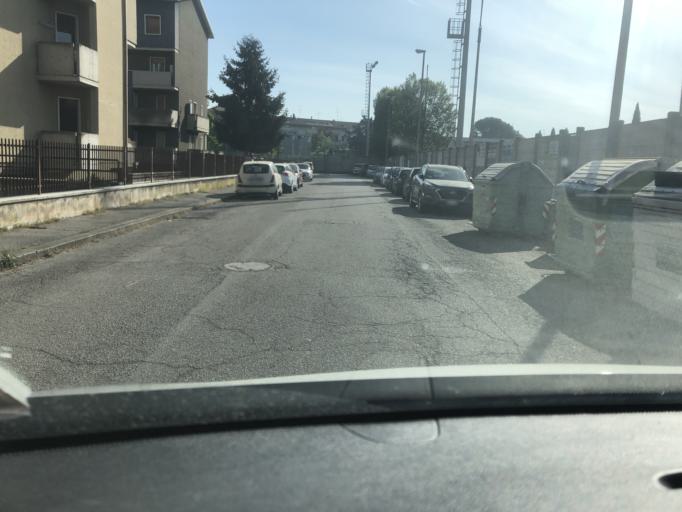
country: IT
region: Veneto
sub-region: Provincia di Verona
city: Poiano
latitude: 45.4345
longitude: 11.0230
